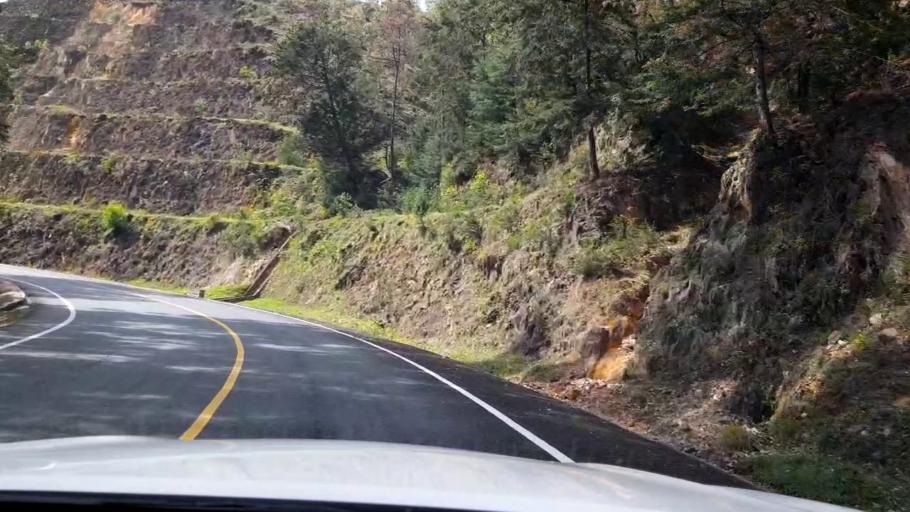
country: RW
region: Southern Province
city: Gitarama
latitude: -2.0320
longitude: 29.7183
